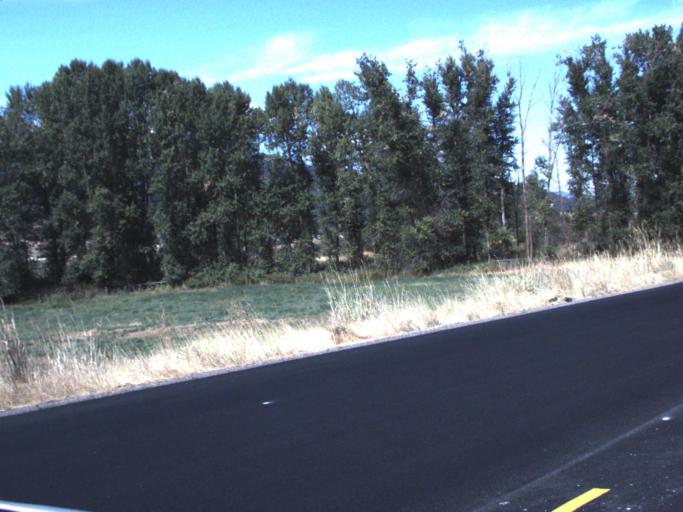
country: US
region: Washington
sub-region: Stevens County
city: Colville
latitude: 48.4851
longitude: -117.9023
